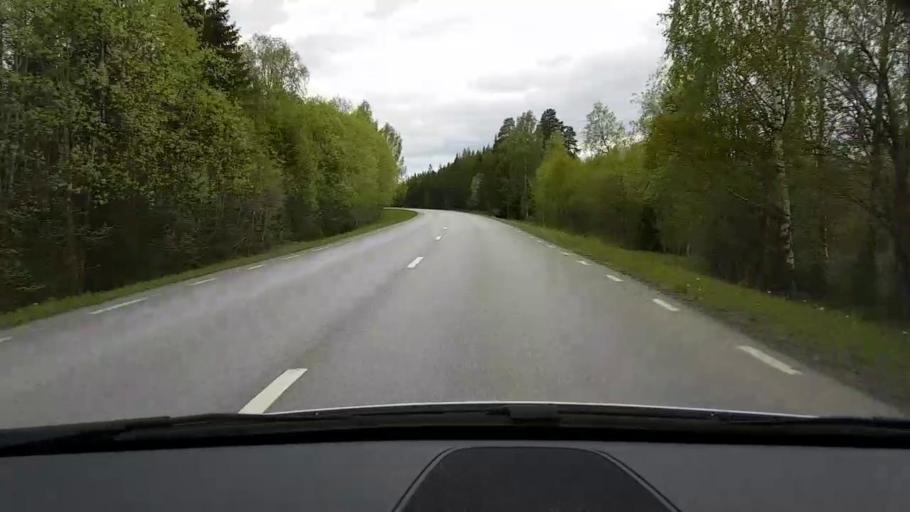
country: SE
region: Jaemtland
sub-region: Krokoms Kommun
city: Valla
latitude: 63.2556
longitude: 13.9931
